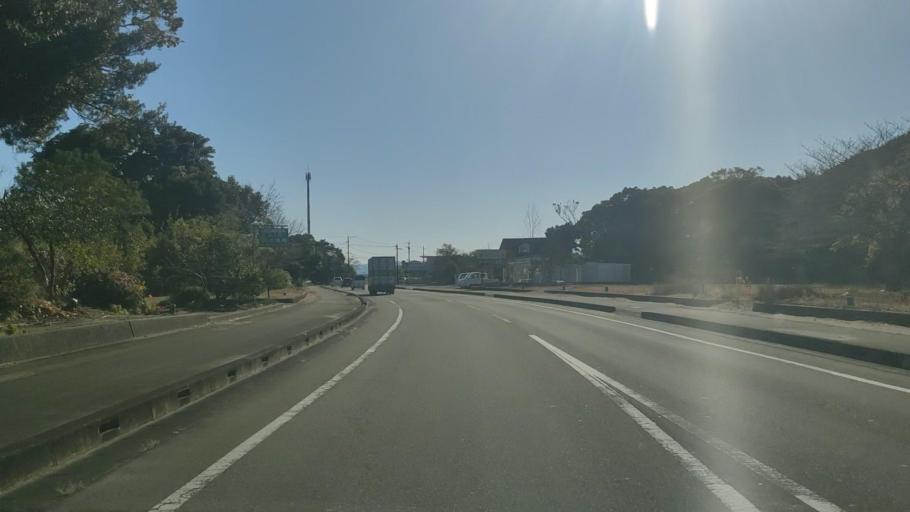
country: JP
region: Miyazaki
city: Miyazaki-shi
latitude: 31.9503
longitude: 131.4601
